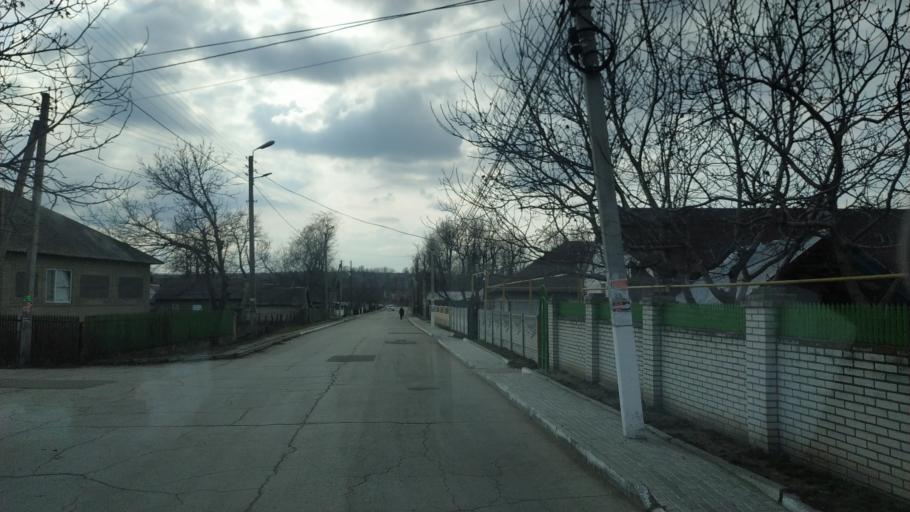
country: MD
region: Anenii Noi
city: Anenii Noi
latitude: 46.9017
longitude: 29.1344
